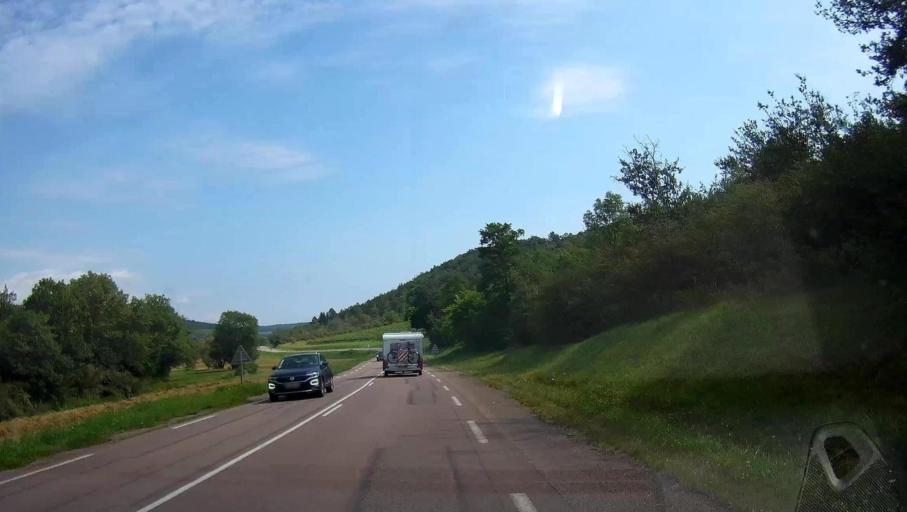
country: FR
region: Bourgogne
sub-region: Departement de la Cote-d'Or
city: Nolay
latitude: 46.9654
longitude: 4.6928
